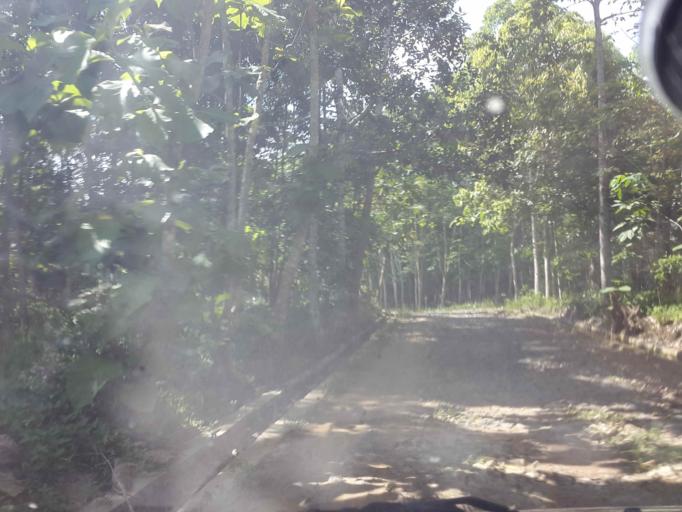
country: ID
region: Lampung
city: Panjang
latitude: -5.4367
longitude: 105.3649
